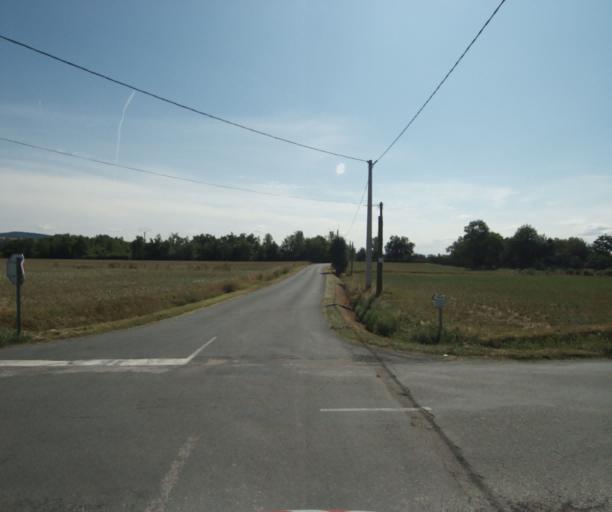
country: FR
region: Midi-Pyrenees
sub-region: Departement de la Haute-Garonne
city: Revel
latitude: 43.4801
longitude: 2.0086
